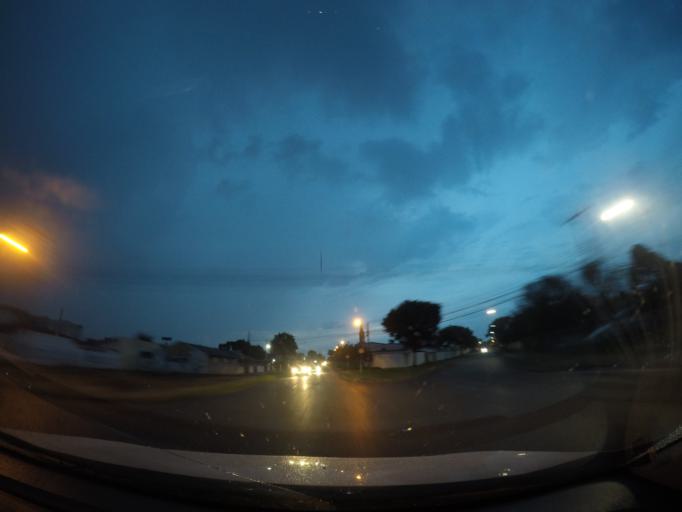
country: BR
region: Parana
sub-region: Sao Jose Dos Pinhais
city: Sao Jose dos Pinhais
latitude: -25.5109
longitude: -49.2289
